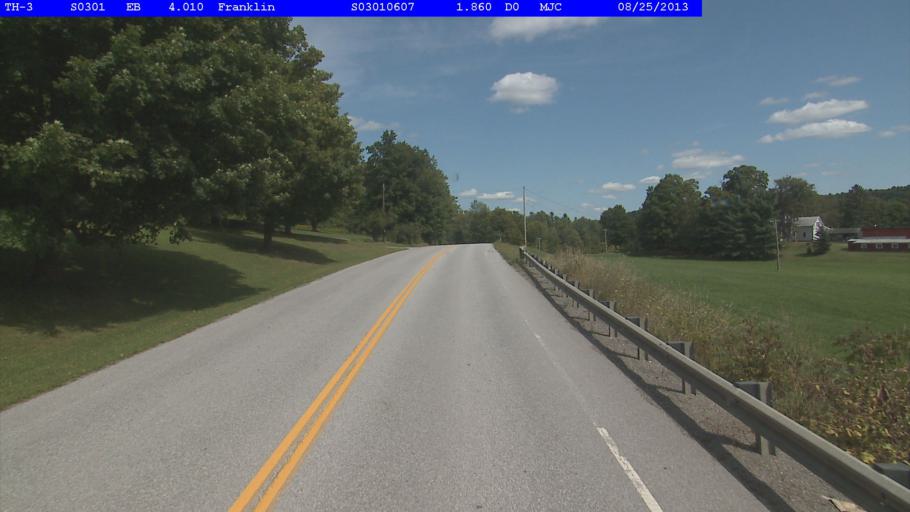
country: CA
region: Quebec
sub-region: Monteregie
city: Bedford
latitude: 44.9733
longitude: -72.9474
